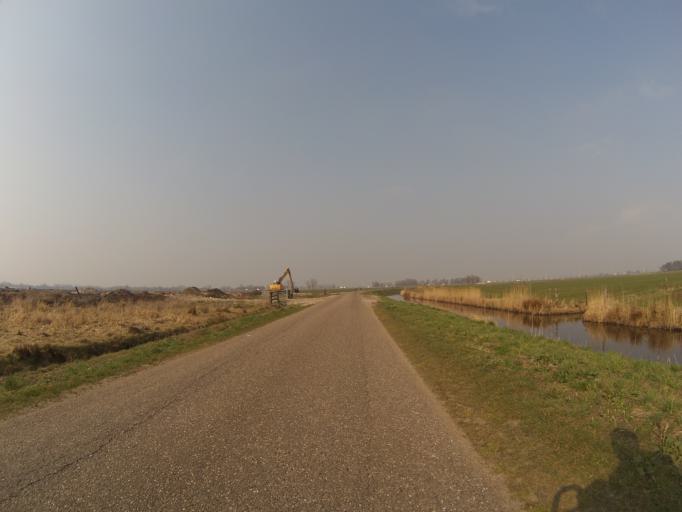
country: NL
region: Utrecht
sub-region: Gemeente Baarn
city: Baarn
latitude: 52.2083
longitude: 5.3282
